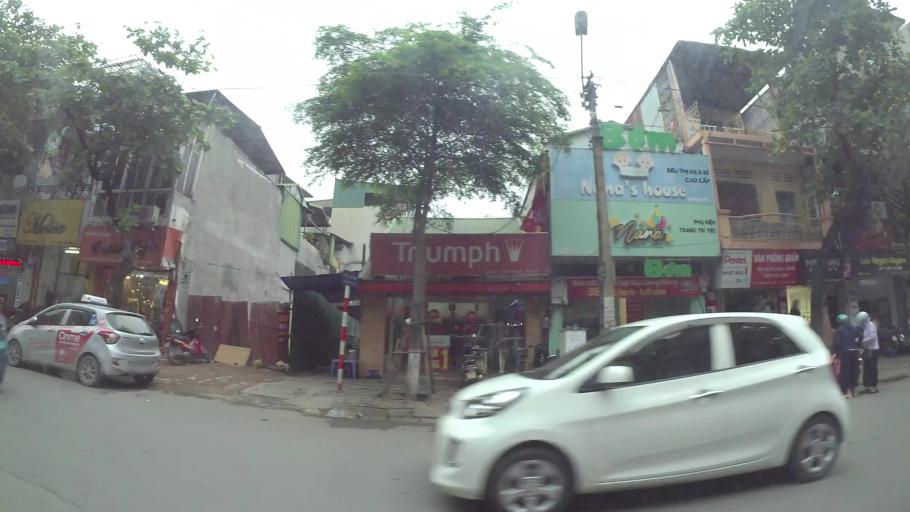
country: VN
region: Ha Noi
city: Dong Da
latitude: 21.0195
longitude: 105.8318
